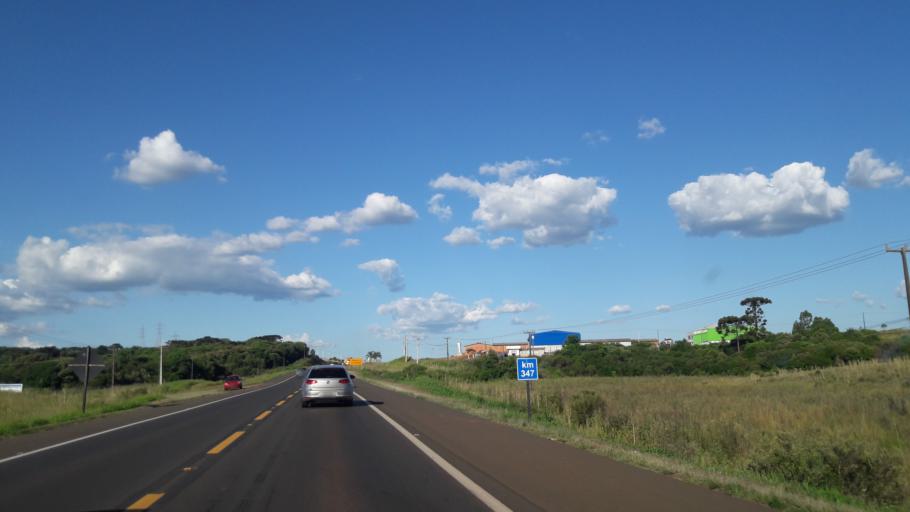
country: BR
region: Parana
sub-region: Guarapuava
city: Guarapuava
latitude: -25.3745
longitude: -51.5019
